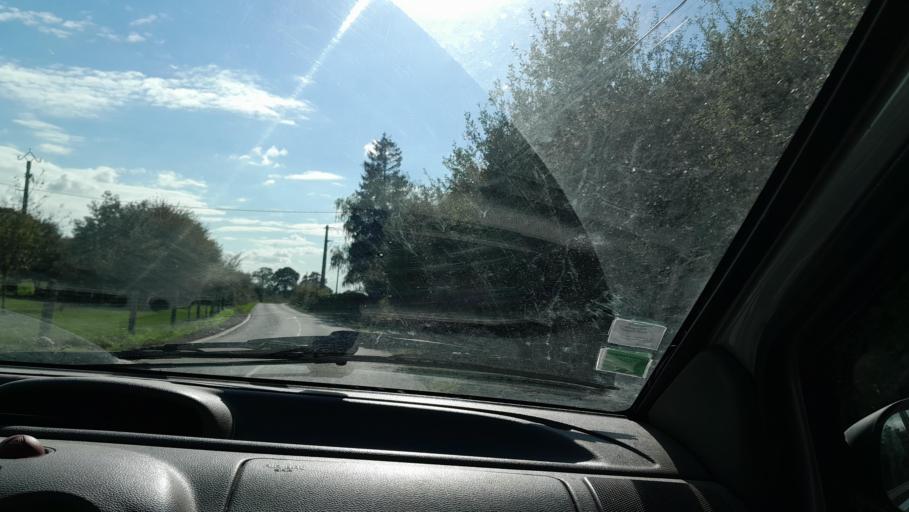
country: FR
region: Pays de la Loire
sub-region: Departement de la Mayenne
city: Ahuille
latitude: 48.0343
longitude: -0.8454
